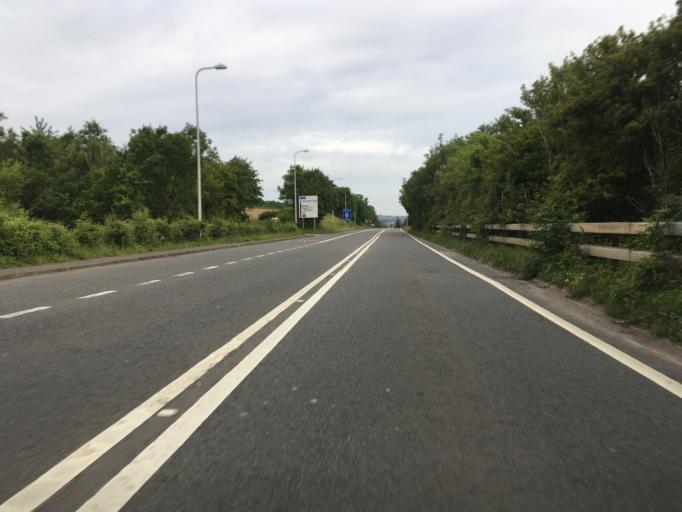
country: GB
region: England
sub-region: North Somerset
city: Easton-in-Gordano
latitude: 51.4739
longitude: -2.7008
